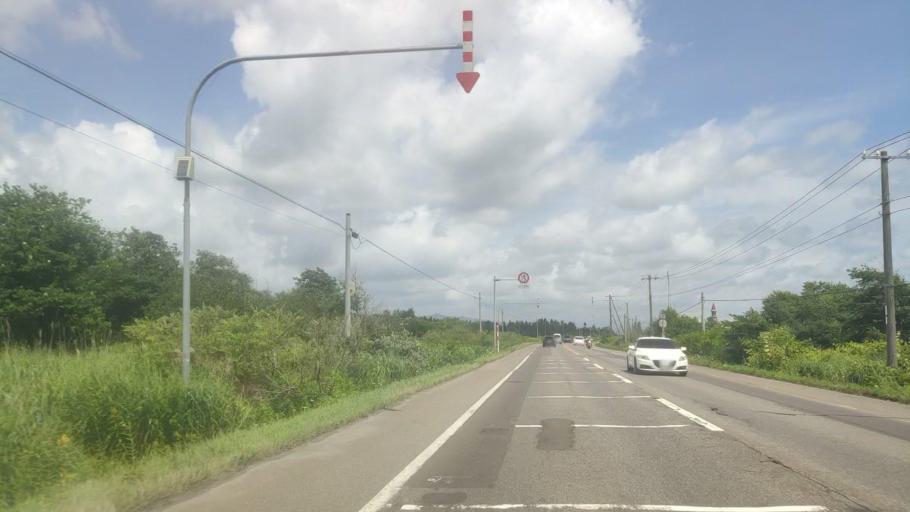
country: JP
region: Hokkaido
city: Niseko Town
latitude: 42.4665
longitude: 140.3403
